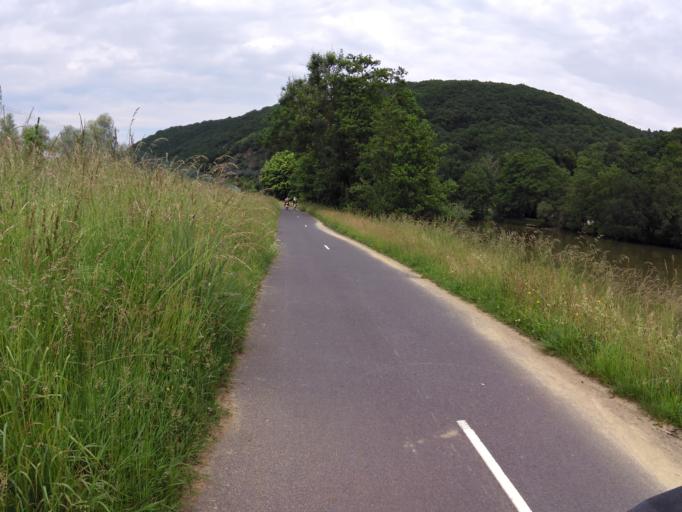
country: FR
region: Champagne-Ardenne
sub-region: Departement des Ardennes
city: Aiglemont
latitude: 49.7974
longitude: 4.7576
